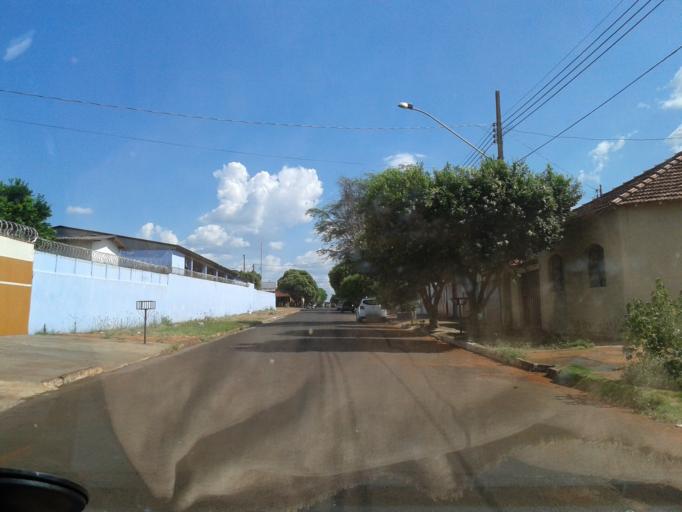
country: BR
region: Minas Gerais
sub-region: Ituiutaba
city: Ituiutaba
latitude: -18.9873
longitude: -49.4691
